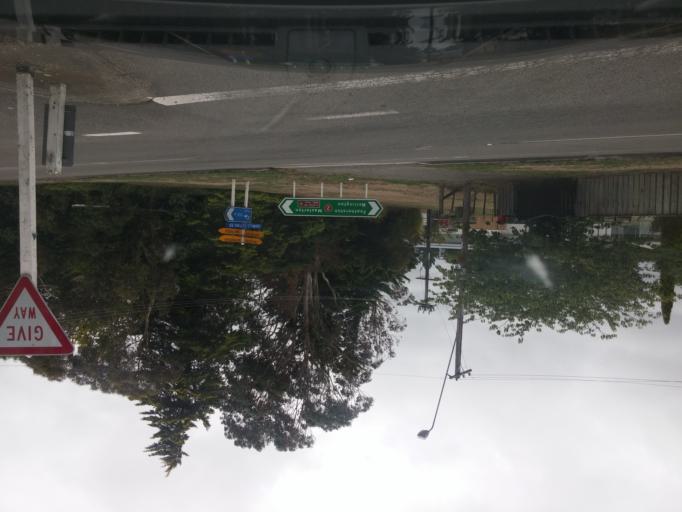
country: NZ
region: Wellington
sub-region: Masterton District
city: Masterton
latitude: -41.0905
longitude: 175.4493
